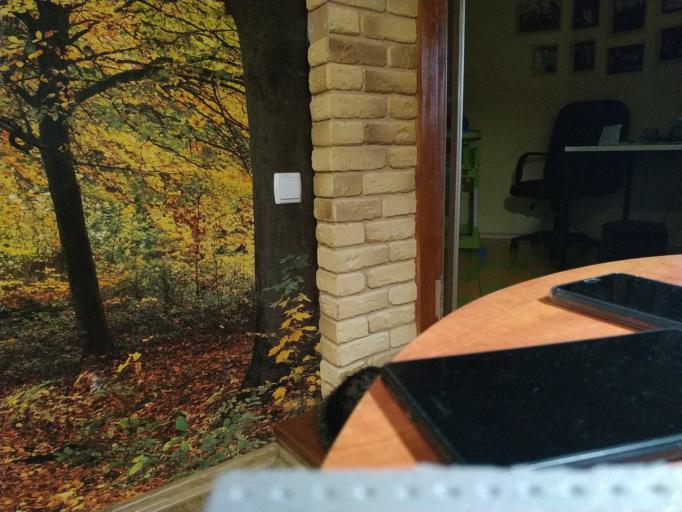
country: RU
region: Tverskaya
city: Zubtsov
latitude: 56.3791
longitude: 34.6581
